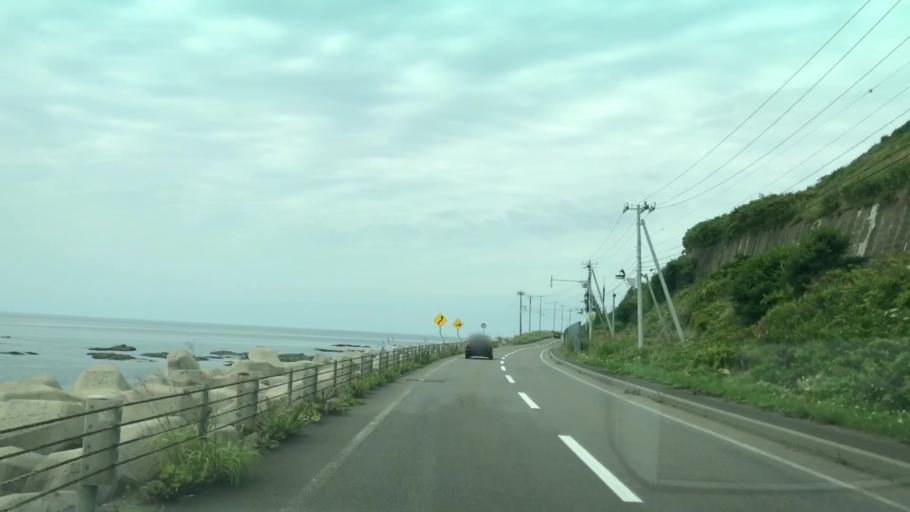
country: JP
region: Hokkaido
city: Iwanai
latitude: 43.1627
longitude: 140.3898
